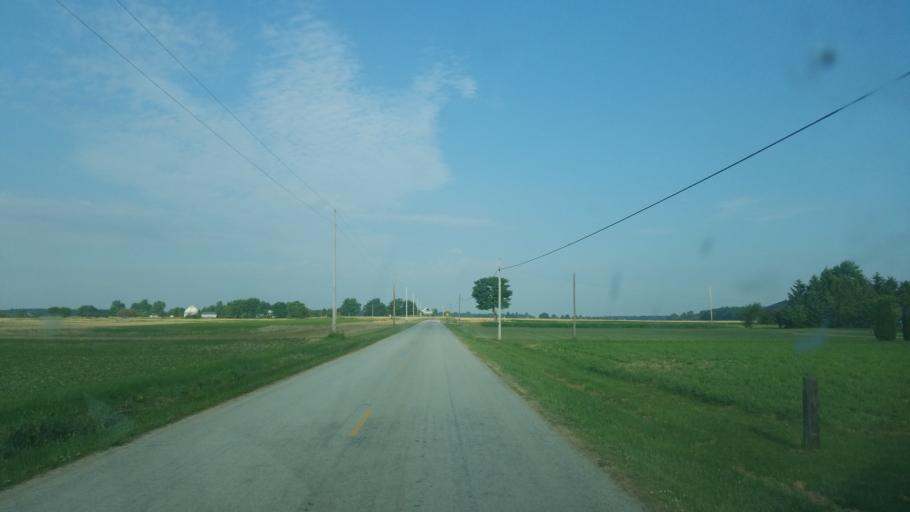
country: US
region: Ohio
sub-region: Hardin County
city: Kenton
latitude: 40.6280
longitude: -83.6983
